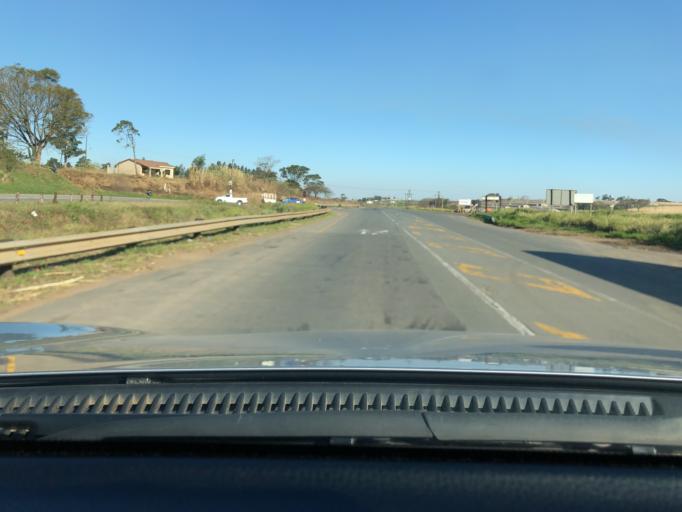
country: ZA
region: KwaZulu-Natal
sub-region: uMgungundlovu District Municipality
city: Camperdown
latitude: -29.7240
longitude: 30.4991
